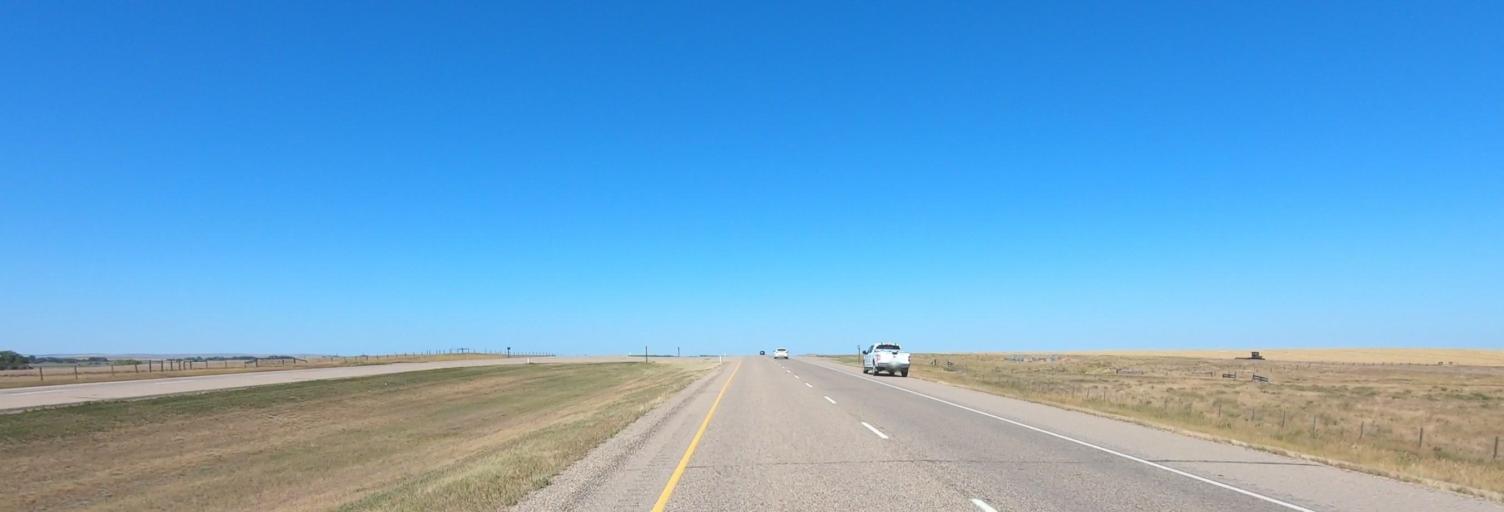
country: CA
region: Alberta
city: Bassano
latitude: 50.7257
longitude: -112.2880
